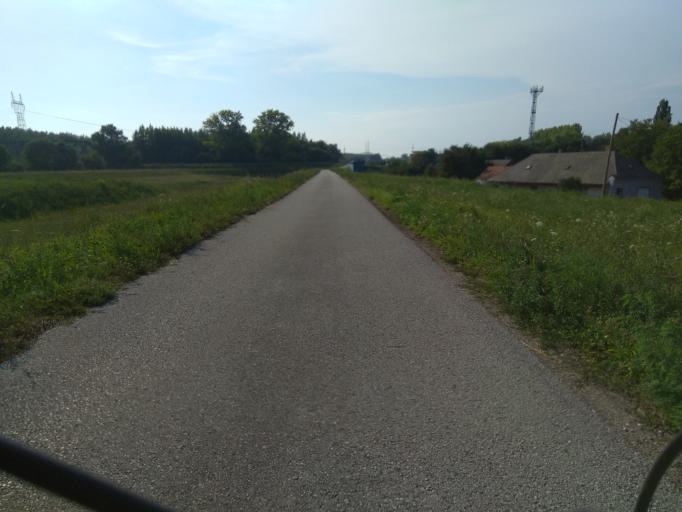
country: HU
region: Gyor-Moson-Sopron
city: Gyor
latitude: 47.7972
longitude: 17.6592
